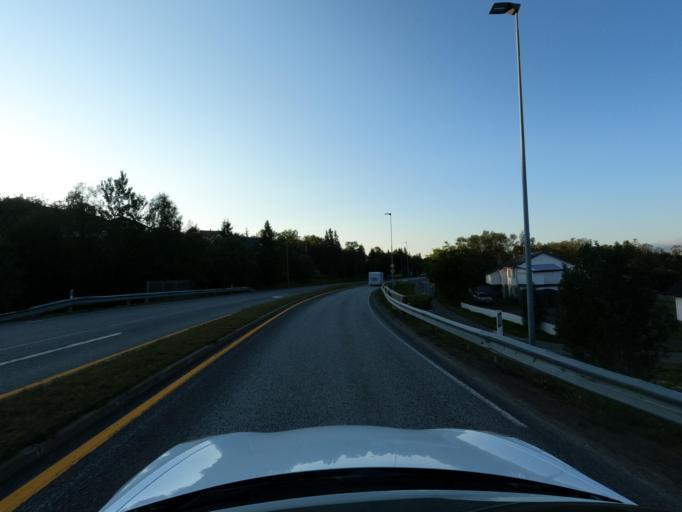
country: NO
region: Troms
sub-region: Harstad
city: Harstad
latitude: 68.7543
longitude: 16.5662
